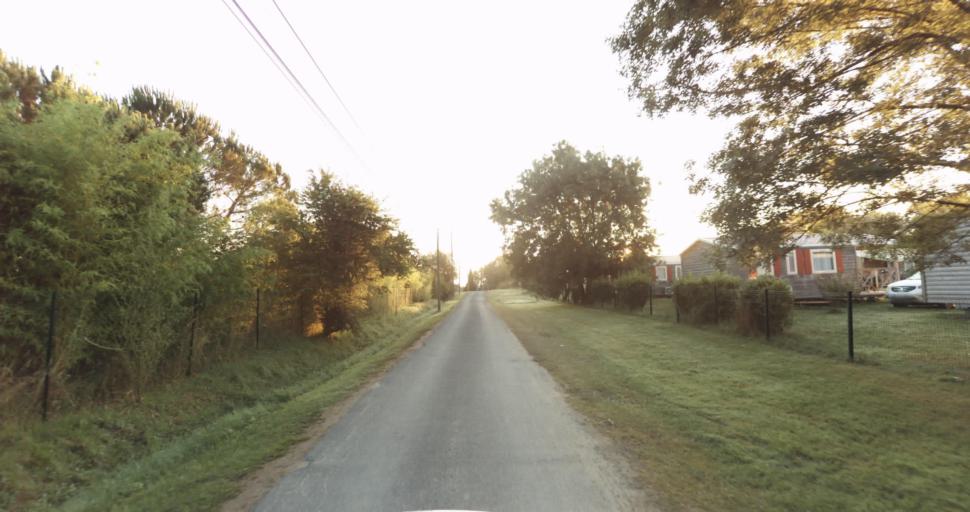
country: FR
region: Aquitaine
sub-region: Departement de la Gironde
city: Bazas
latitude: 44.4265
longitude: -0.1981
